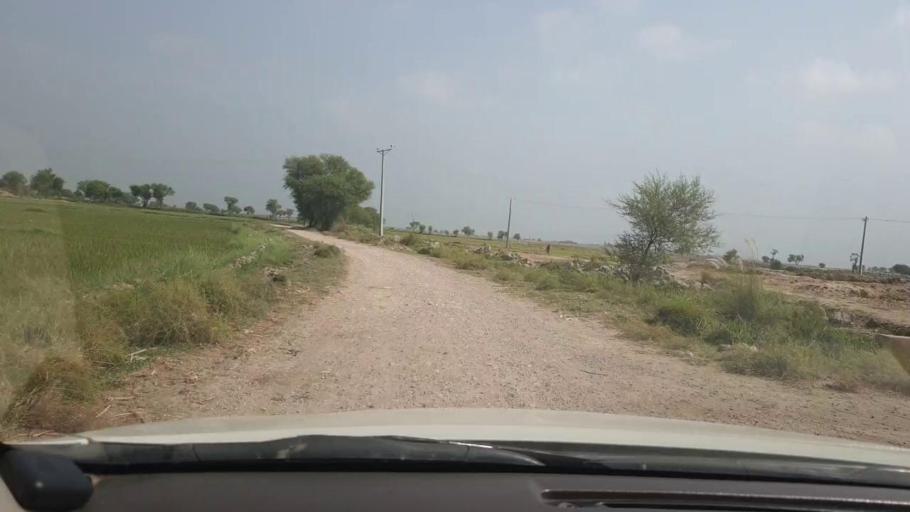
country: PK
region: Sindh
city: Shikarpur
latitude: 28.0164
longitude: 68.5937
